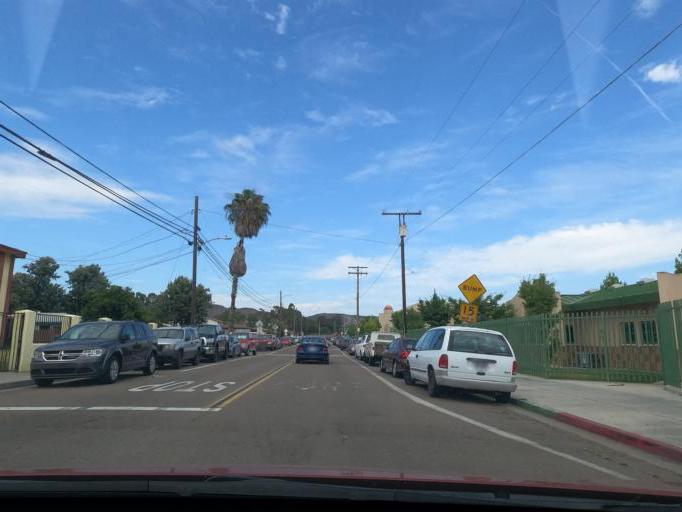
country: US
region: California
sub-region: San Diego County
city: Imperial Beach
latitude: 32.5582
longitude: -117.0514
